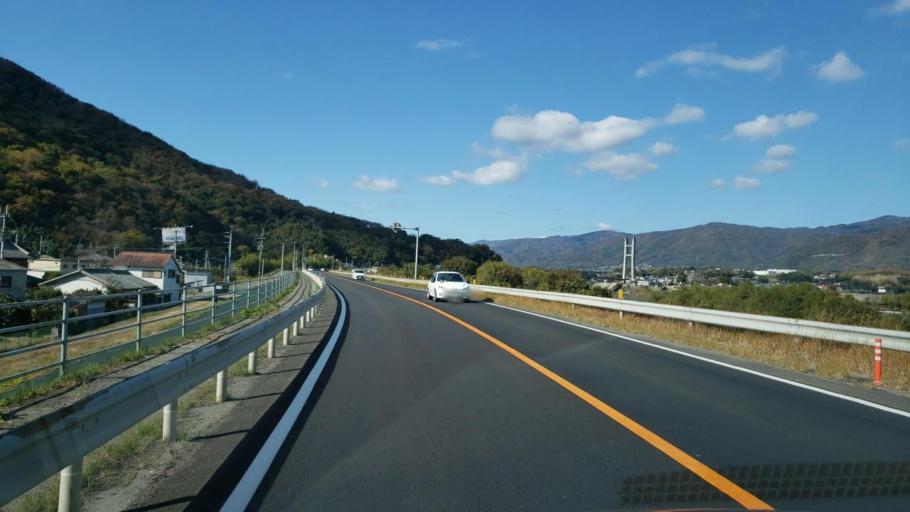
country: JP
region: Tokushima
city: Wakimachi
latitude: 34.0624
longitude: 134.2035
